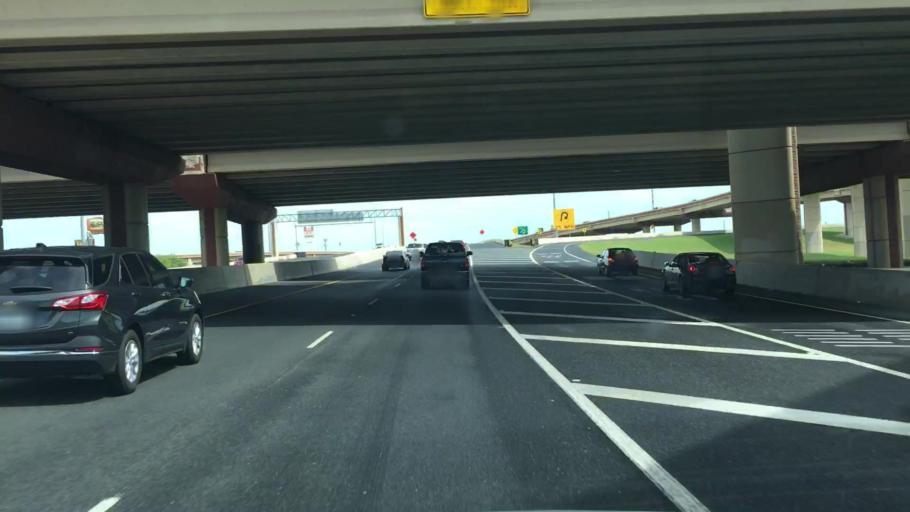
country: US
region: Texas
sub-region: Nueces County
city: Corpus Christi
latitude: 27.7373
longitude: -97.4308
